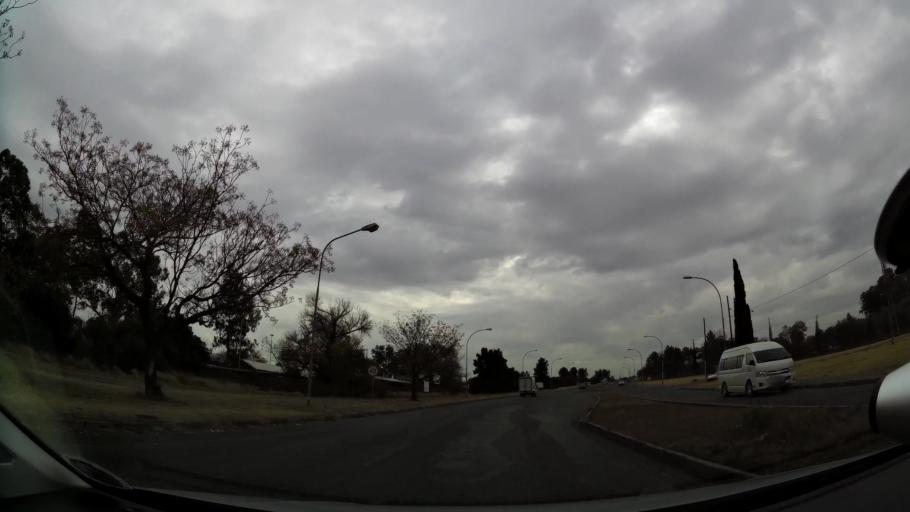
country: ZA
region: Orange Free State
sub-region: Fezile Dabi District Municipality
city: Kroonstad
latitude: -27.6577
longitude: 27.2302
